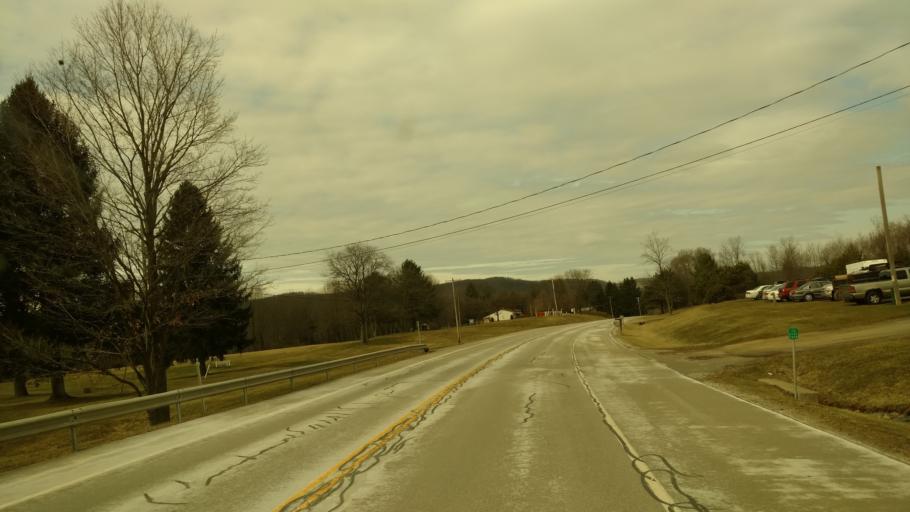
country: US
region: New York
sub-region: Allegany County
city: Wellsville
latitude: 42.0390
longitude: -77.9134
